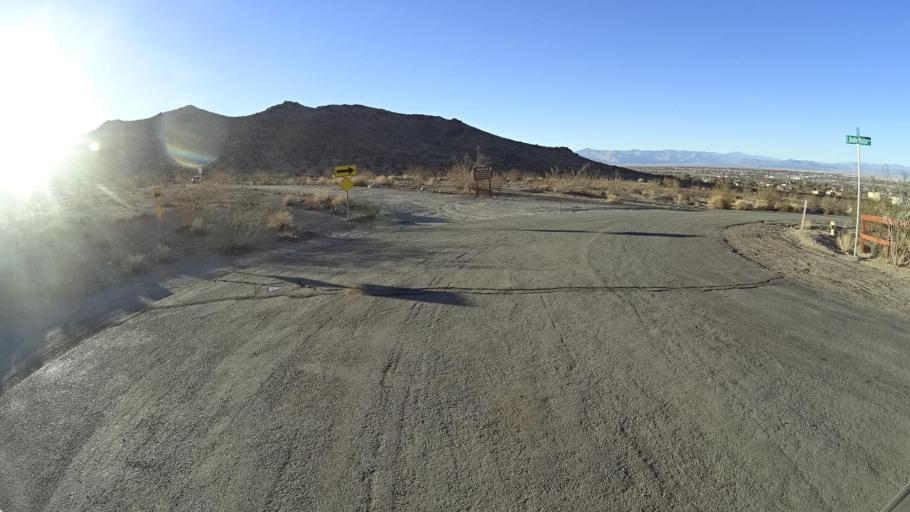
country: US
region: California
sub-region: Kern County
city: Ridgecrest
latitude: 35.5729
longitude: -117.6522
